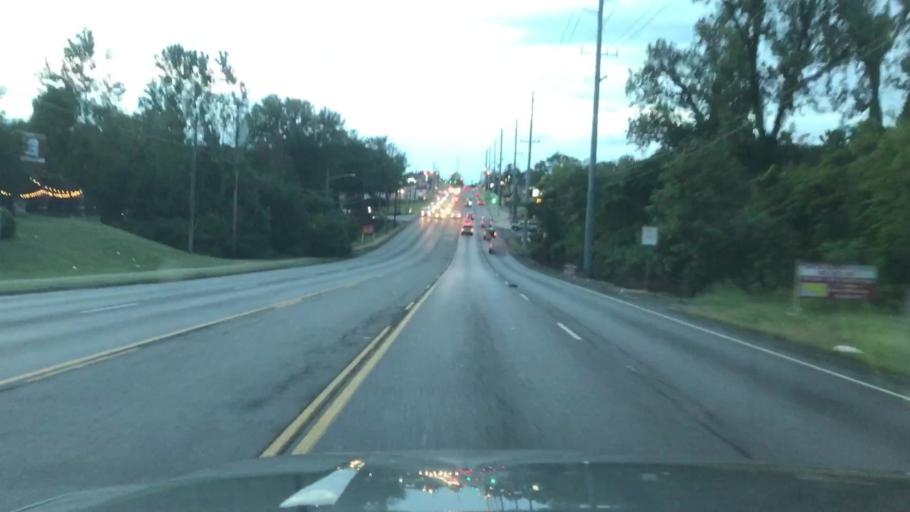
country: US
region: Tennessee
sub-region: Rutherford County
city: La Vergne
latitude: 36.0896
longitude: -86.6503
